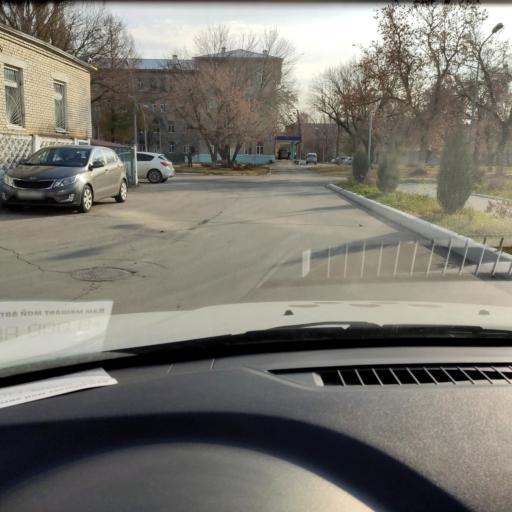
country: RU
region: Samara
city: Tol'yatti
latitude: 53.5036
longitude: 49.4102
